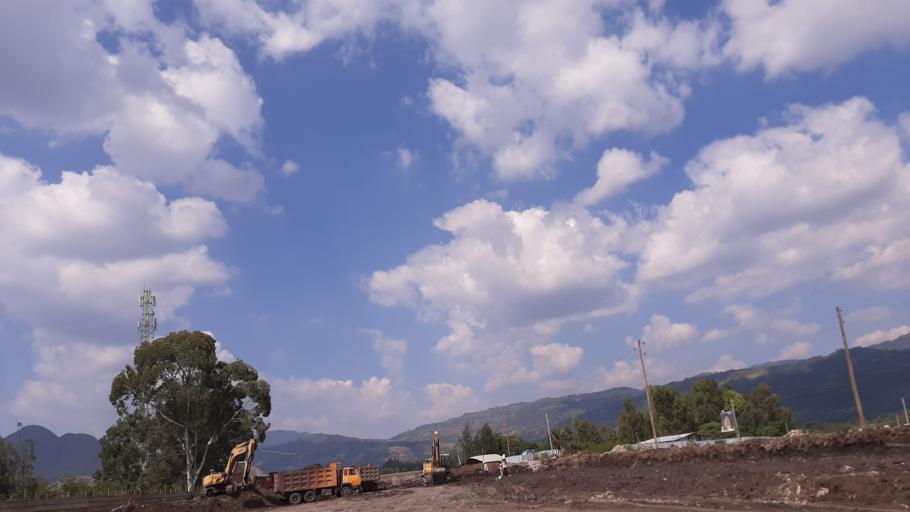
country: ET
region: Amhara
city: Kombolcha
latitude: 11.0937
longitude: 39.7134
